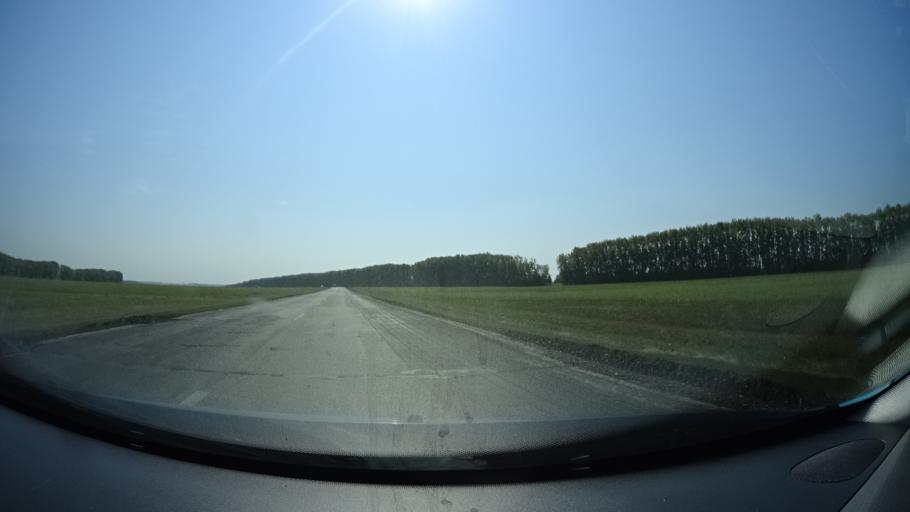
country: RU
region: Bashkortostan
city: Kabakovo
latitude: 54.4548
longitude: 55.9707
